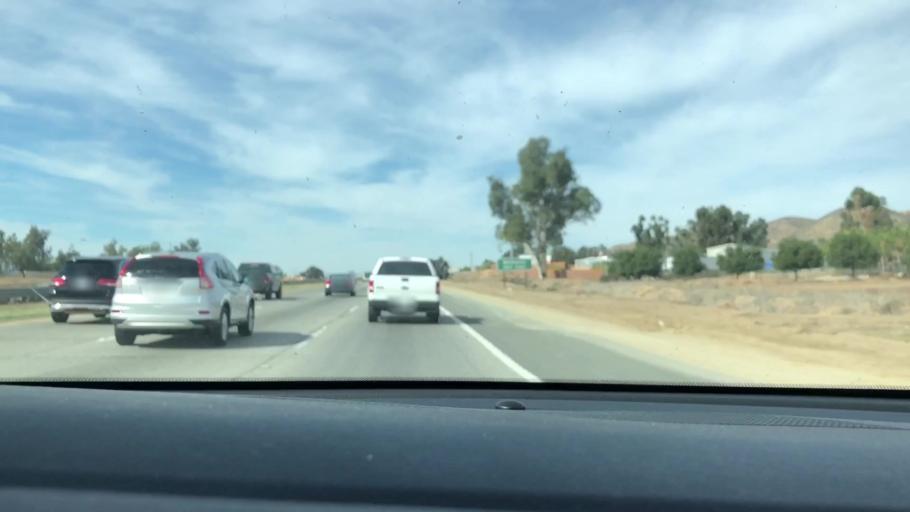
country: US
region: California
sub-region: Riverside County
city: Wildomar
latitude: 33.6042
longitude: -117.2523
